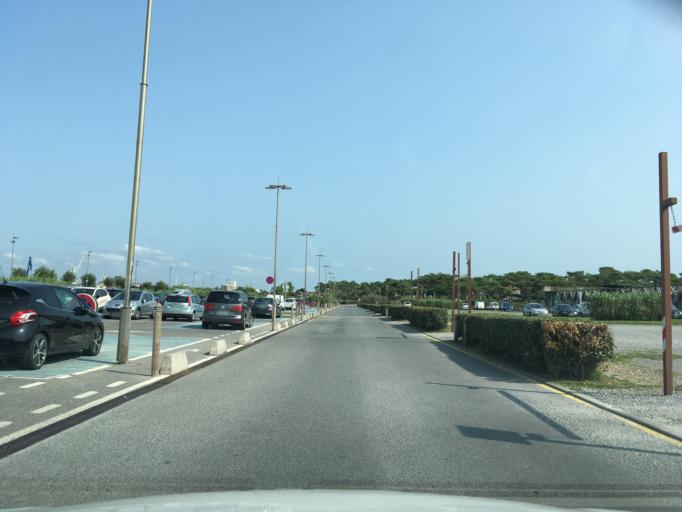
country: FR
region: Aquitaine
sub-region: Departement des Pyrenees-Atlantiques
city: Anglet
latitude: 43.5269
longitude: -1.5207
